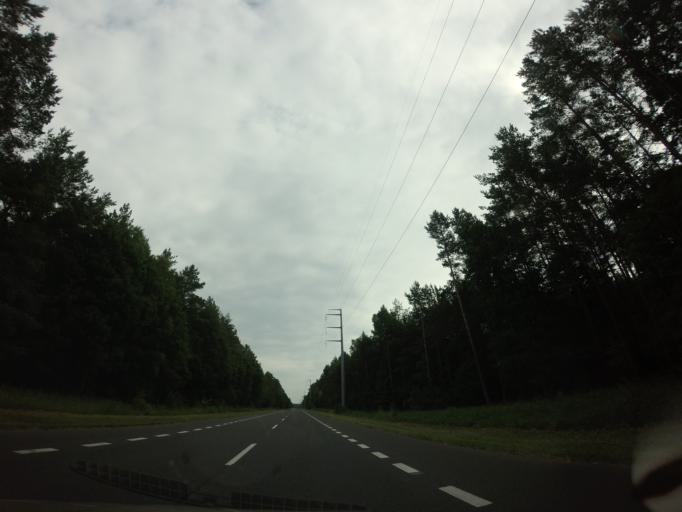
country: PL
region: West Pomeranian Voivodeship
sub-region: Powiat walecki
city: Miroslawiec
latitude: 53.3829
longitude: 16.1513
